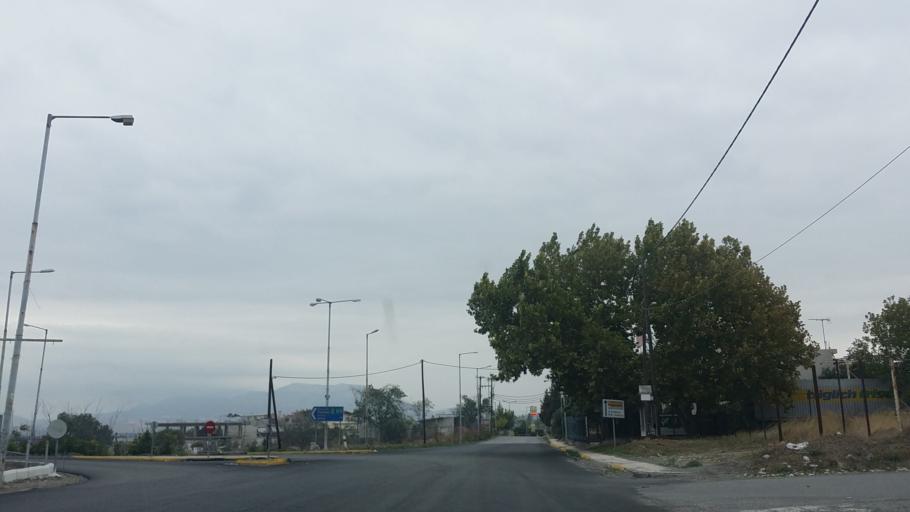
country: GR
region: Central Greece
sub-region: Nomos Voiotias
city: Thivai
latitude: 38.3284
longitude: 23.3028
